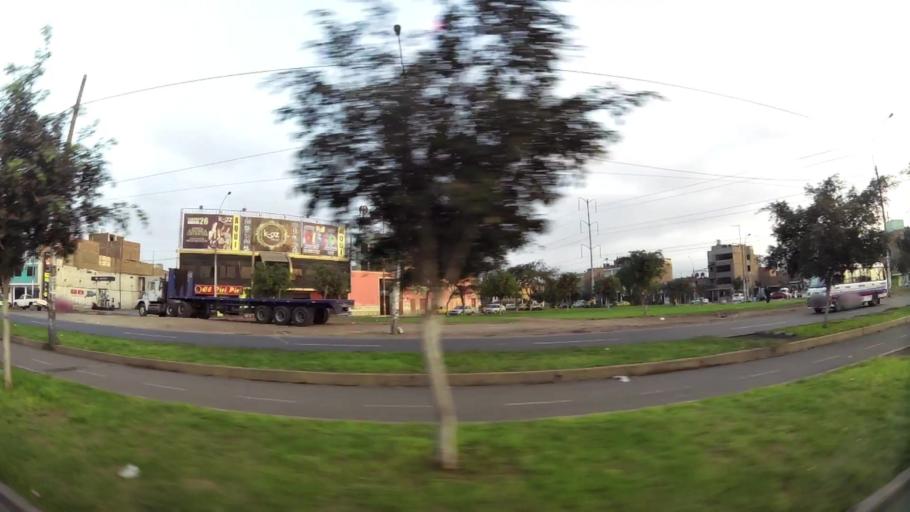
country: PE
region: Lima
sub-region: Lima
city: Independencia
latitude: -12.0123
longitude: -77.0867
